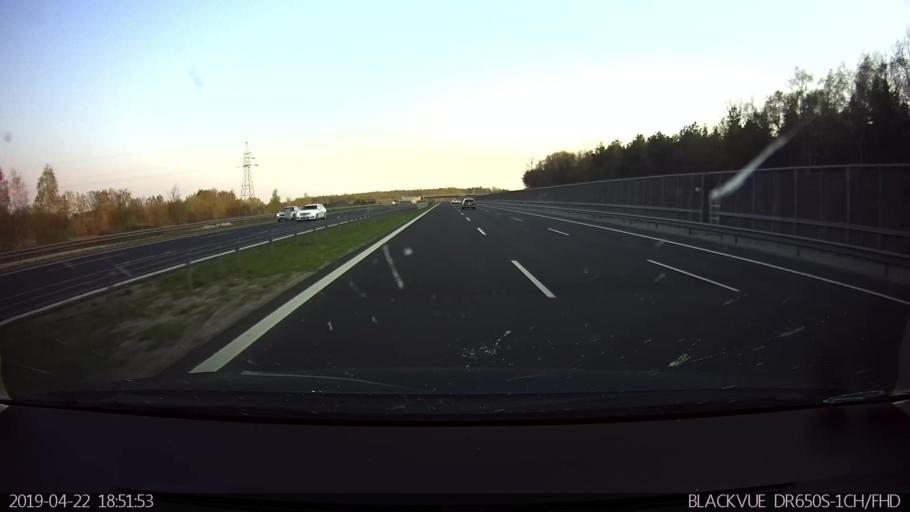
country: PL
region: Masovian Voivodeship
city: Zielonka
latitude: 52.3360
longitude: 21.1572
